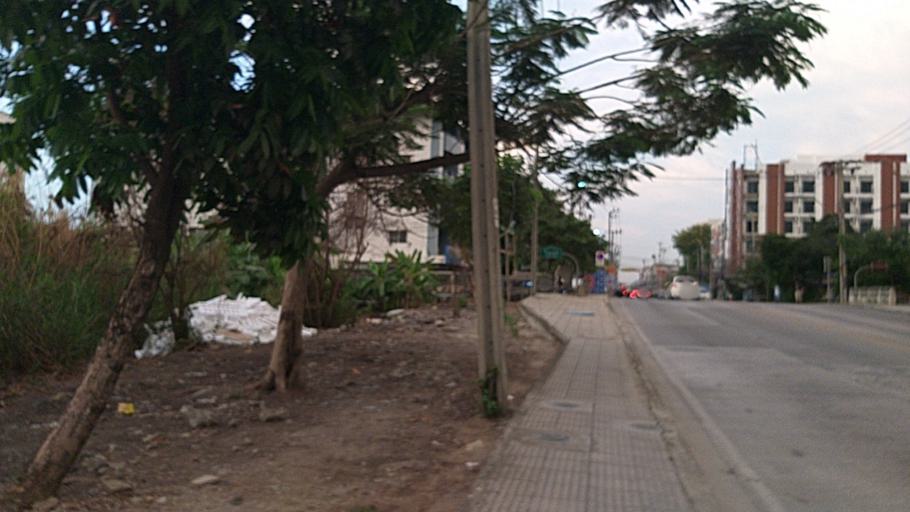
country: TH
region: Bangkok
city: Bang Na
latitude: 13.6656
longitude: 100.6827
